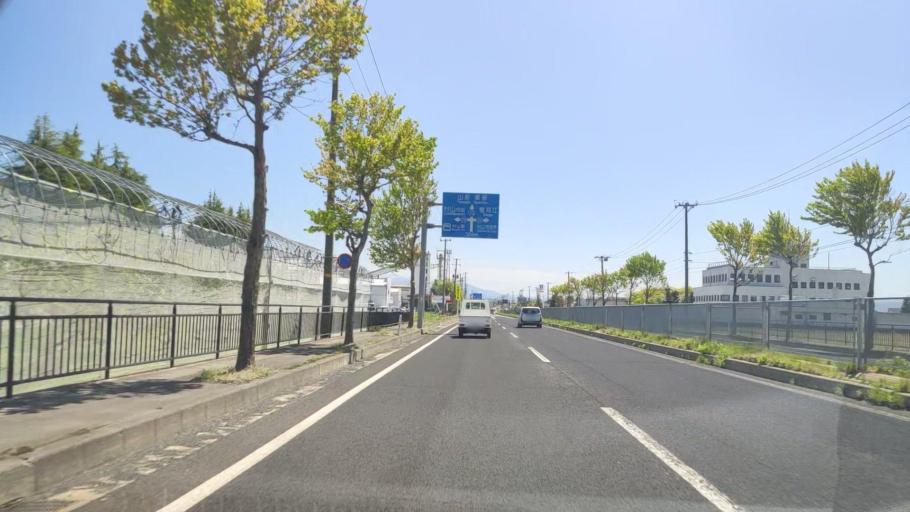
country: JP
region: Yamagata
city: Higashine
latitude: 38.4855
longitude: 140.3831
